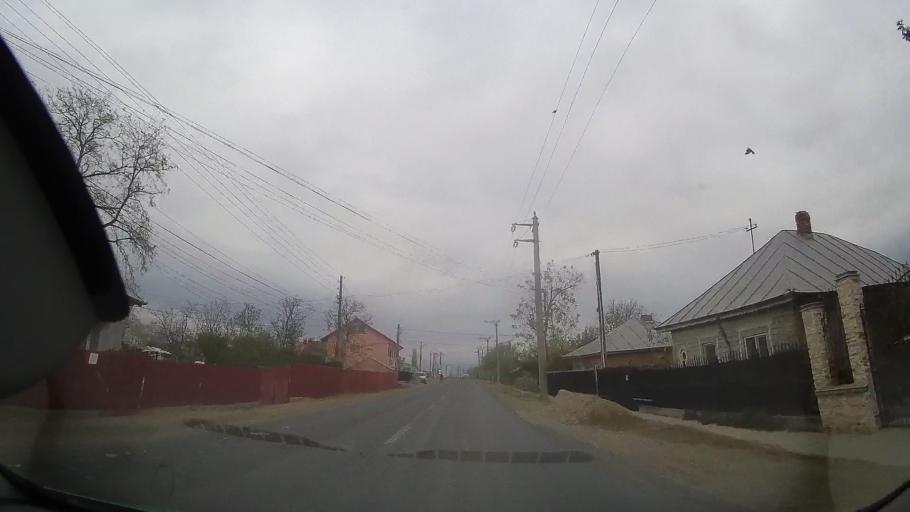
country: RO
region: Buzau
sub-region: Comuna Padina
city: Padina
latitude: 44.8227
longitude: 27.1152
